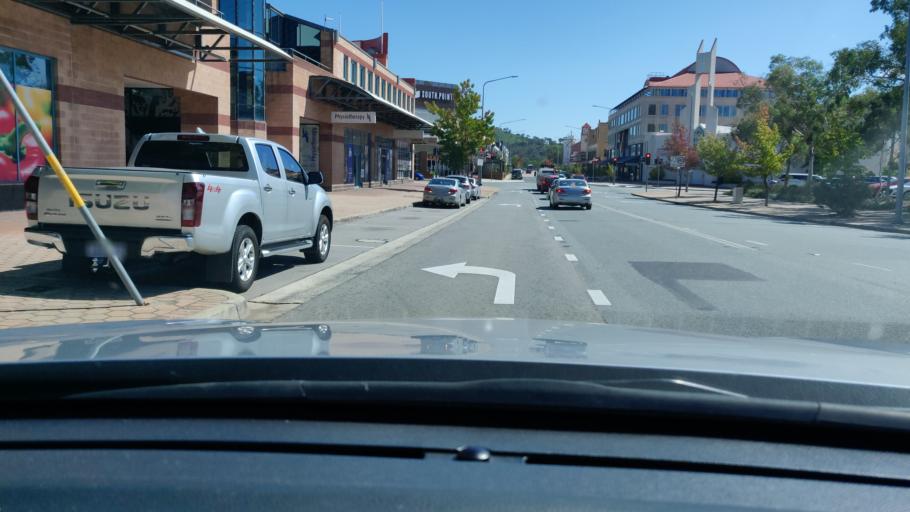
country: AU
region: Australian Capital Territory
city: Macarthur
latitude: -35.4177
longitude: 149.0691
